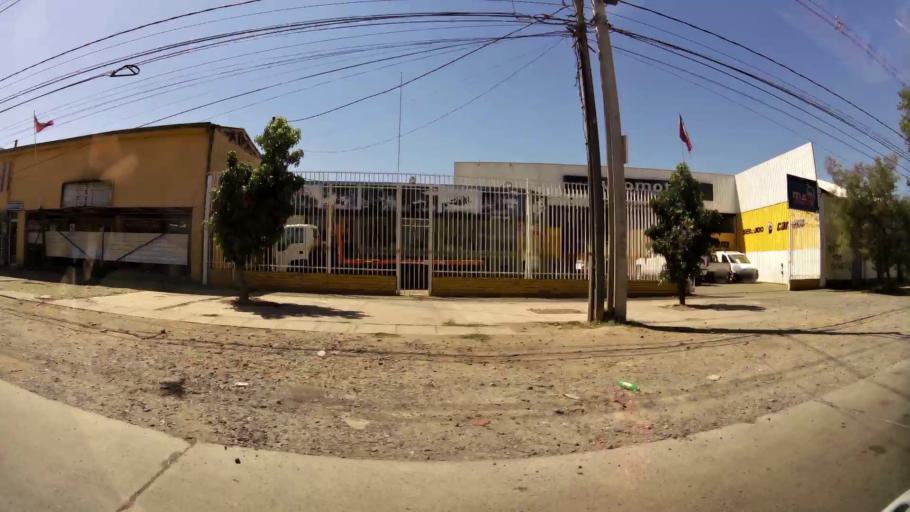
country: CL
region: Maule
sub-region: Provincia de Talca
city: Talca
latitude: -35.4157
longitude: -71.6567
